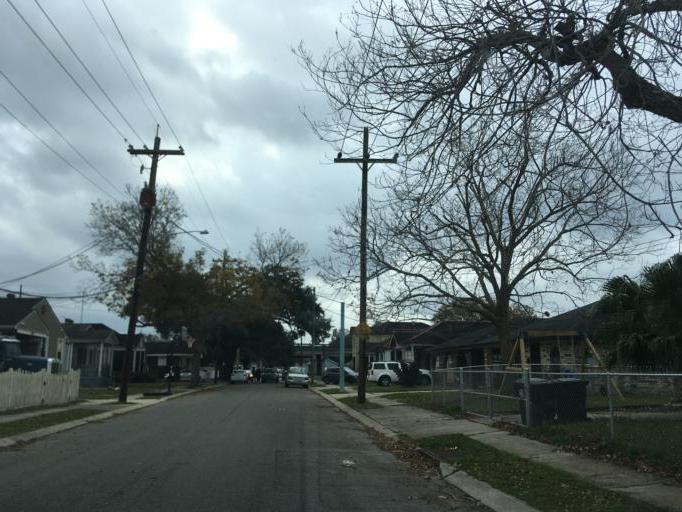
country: US
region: Louisiana
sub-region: Orleans Parish
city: New Orleans
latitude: 29.9927
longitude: -90.0612
